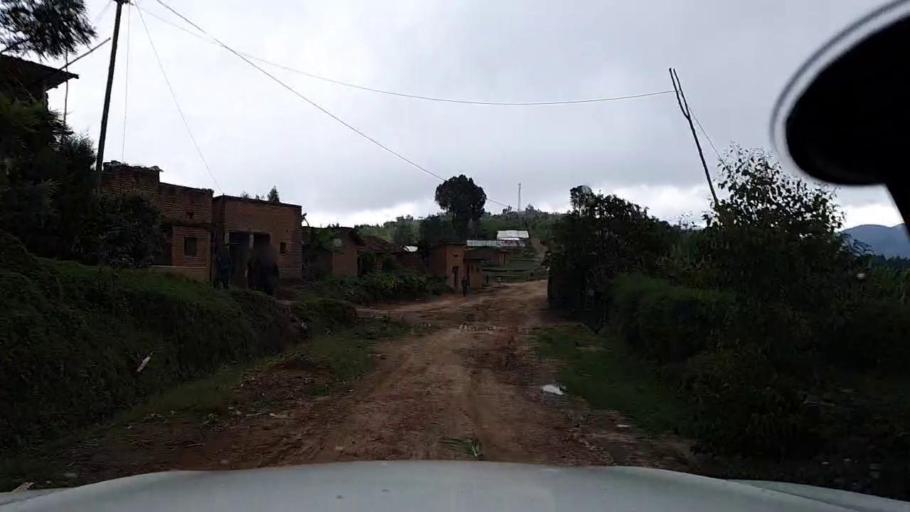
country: RW
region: Western Province
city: Kibuye
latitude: -2.0902
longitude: 29.4965
